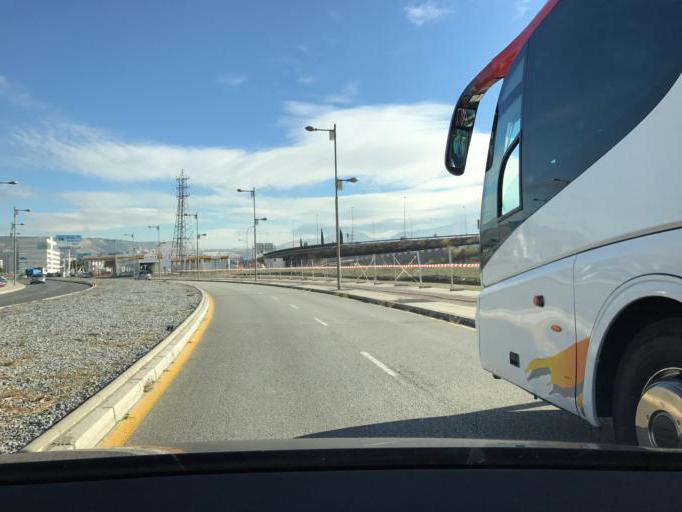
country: ES
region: Andalusia
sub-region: Provincia de Granada
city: Armilla
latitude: 37.1447
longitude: -3.6048
